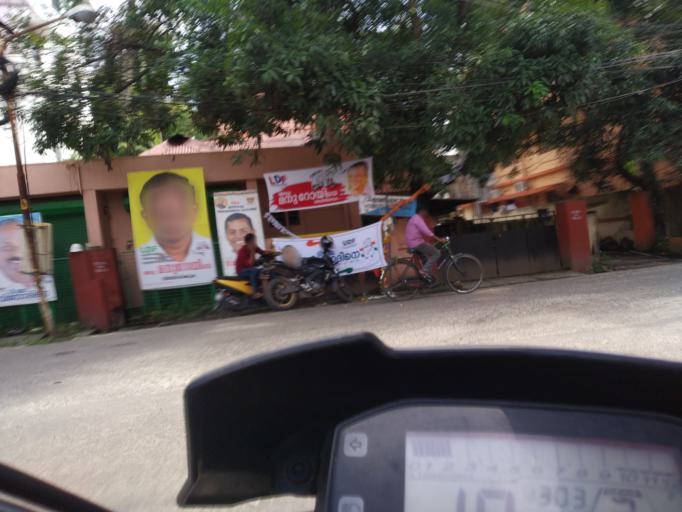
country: IN
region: Kerala
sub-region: Ernakulam
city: Cochin
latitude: 9.9850
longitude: 76.2861
